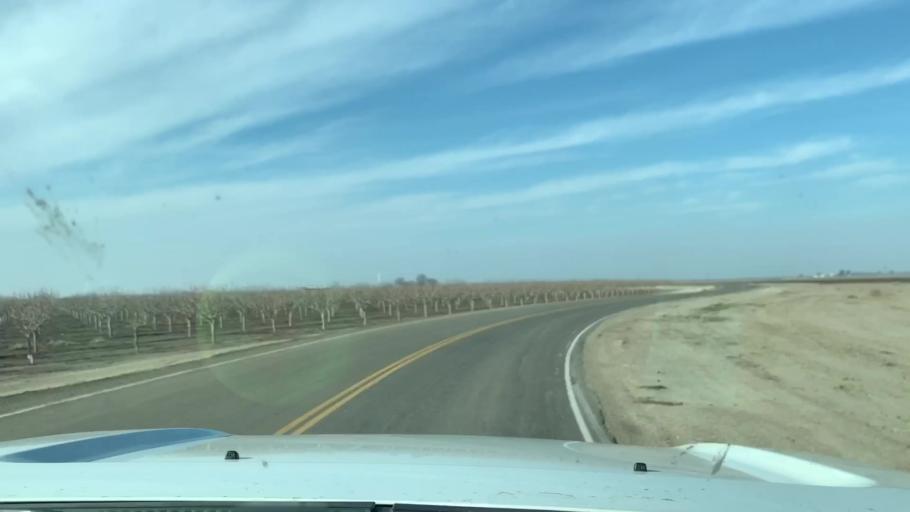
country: US
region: California
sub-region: Kern County
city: Buttonwillow
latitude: 35.4501
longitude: -119.5613
